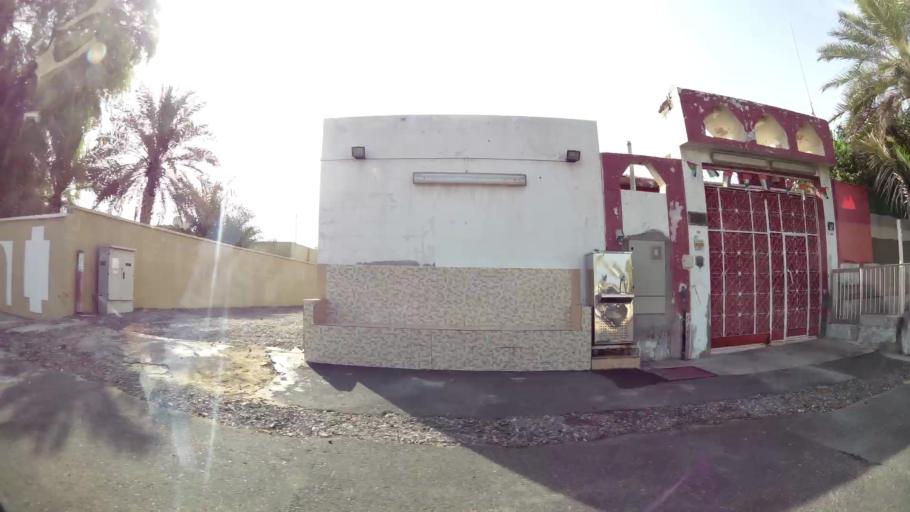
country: AE
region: Ash Shariqah
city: Sharjah
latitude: 25.2219
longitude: 55.4013
